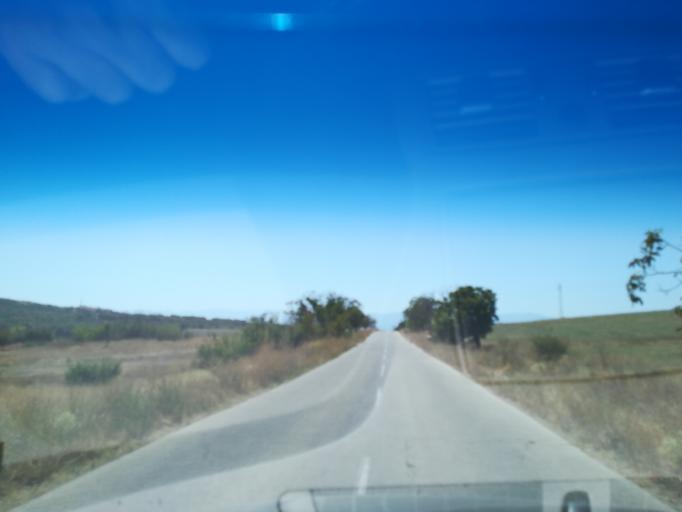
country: BG
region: Pazardzhik
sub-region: Obshtina Pazardzhik
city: Pazardzhik
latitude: 42.3173
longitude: 24.4063
